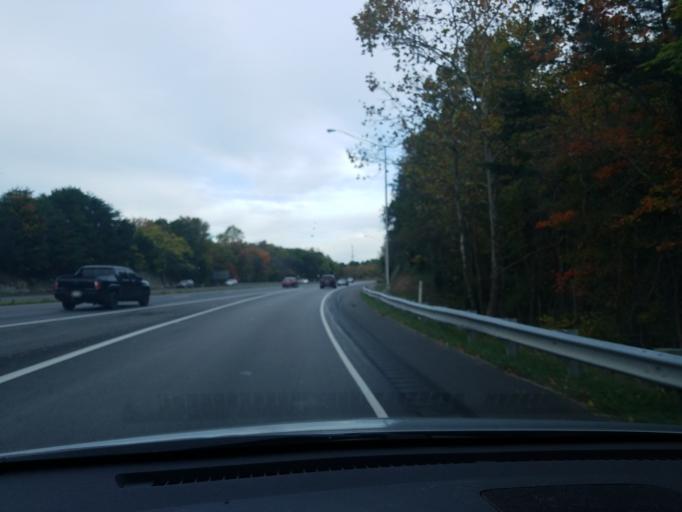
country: US
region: Indiana
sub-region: Floyd County
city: New Albany
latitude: 38.3039
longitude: -85.8844
